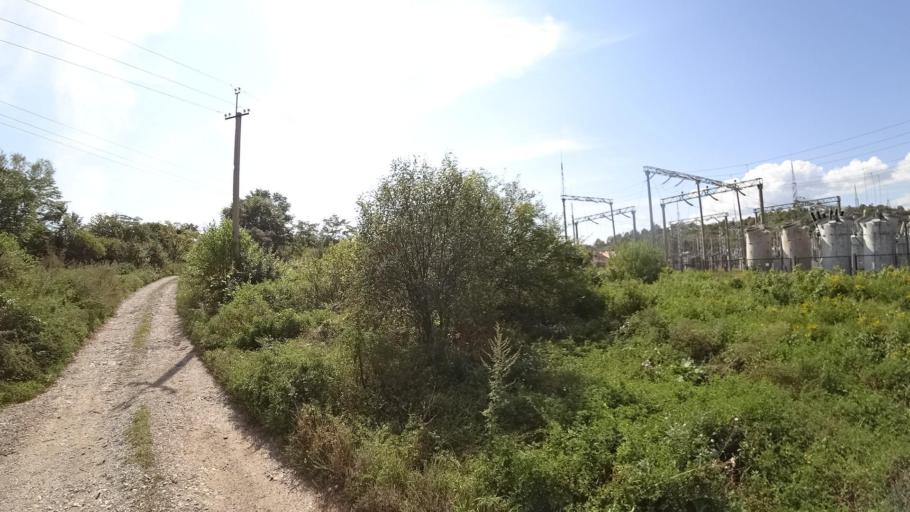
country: RU
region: Jewish Autonomous Oblast
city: Londoko
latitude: 49.0139
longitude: 131.8983
